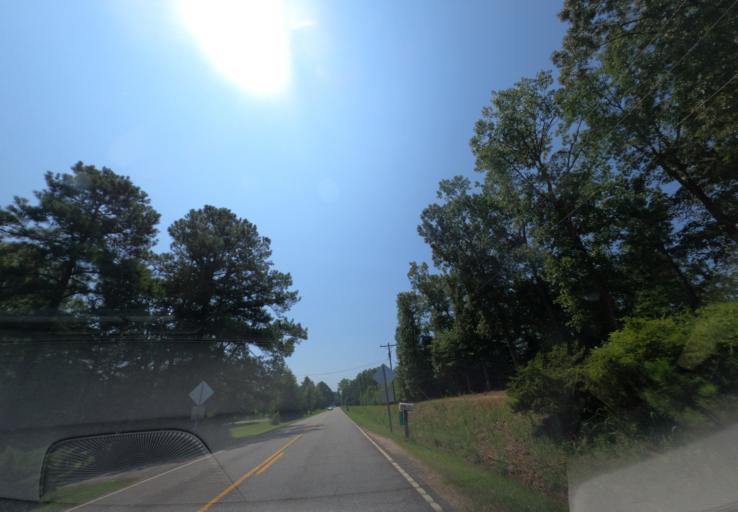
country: US
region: South Carolina
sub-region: Greenwood County
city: Greenwood
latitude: 34.0468
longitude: -82.1347
